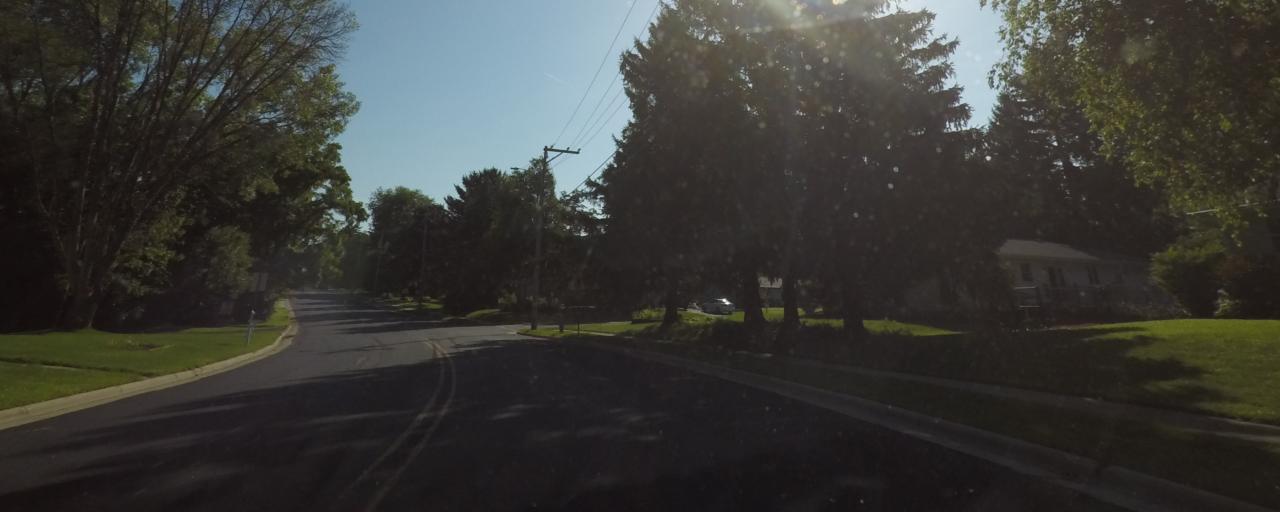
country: US
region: Wisconsin
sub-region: Dane County
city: McFarland
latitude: 43.0061
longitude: -89.2992
